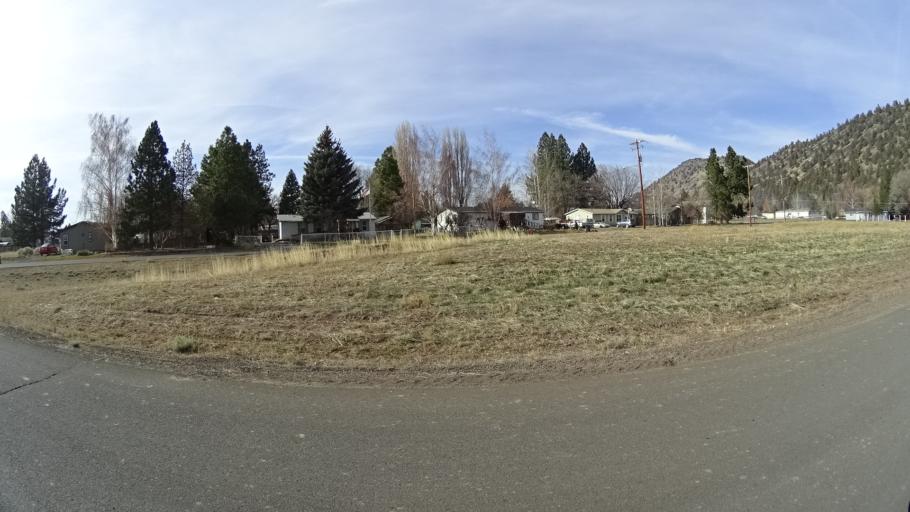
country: US
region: Oregon
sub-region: Klamath County
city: Klamath Falls
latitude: 41.9691
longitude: -121.9139
